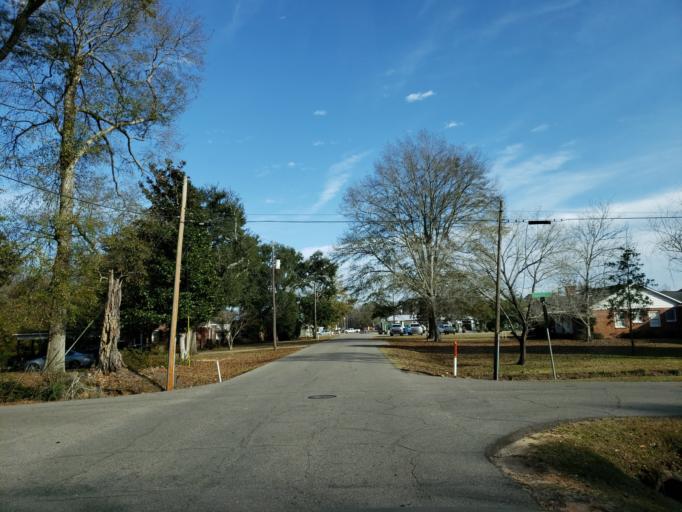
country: US
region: Mississippi
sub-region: Perry County
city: Richton
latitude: 31.3500
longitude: -88.9380
